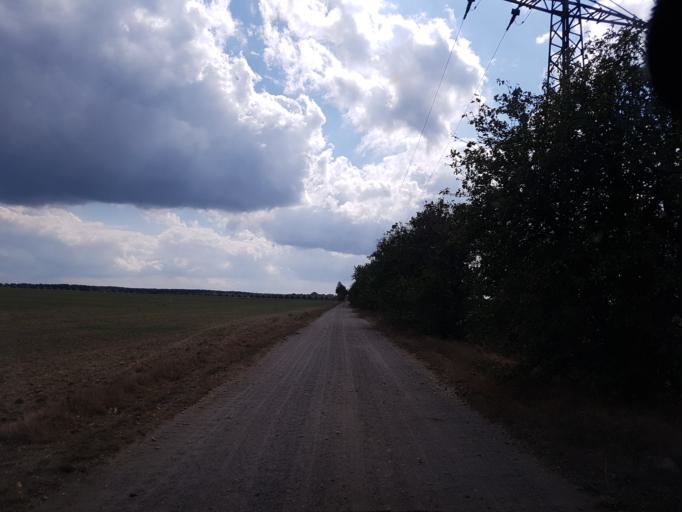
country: DE
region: Brandenburg
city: Finsterwalde
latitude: 51.6271
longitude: 13.7540
